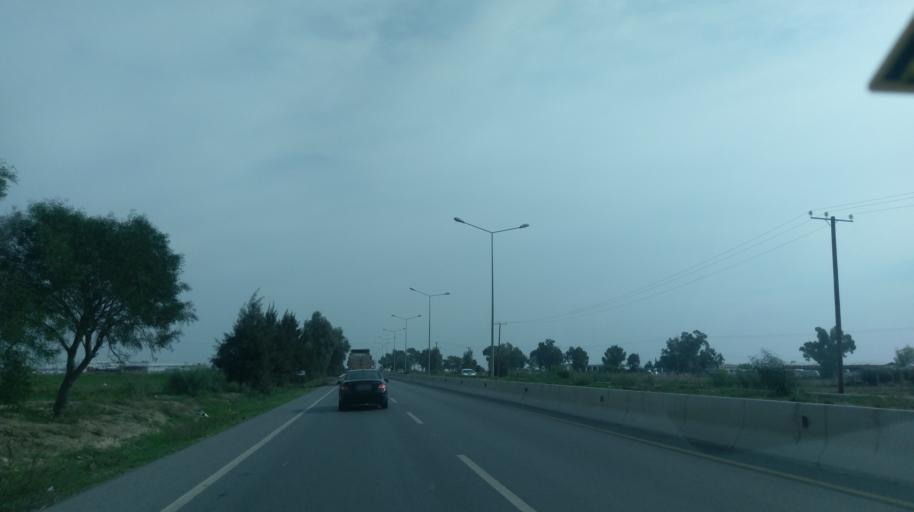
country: CY
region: Lefkosia
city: Nicosia
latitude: 35.2142
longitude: 33.4406
